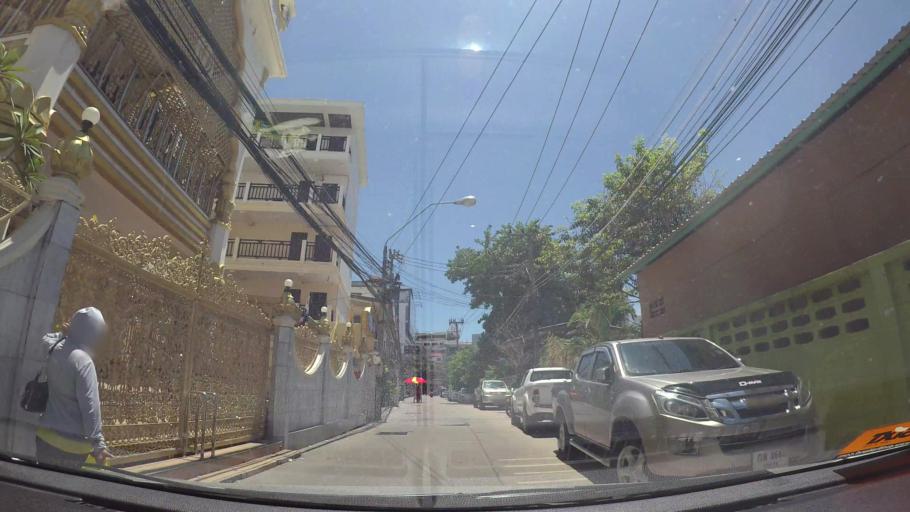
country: TH
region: Chon Buri
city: Phatthaya
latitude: 12.9248
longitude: 100.8749
